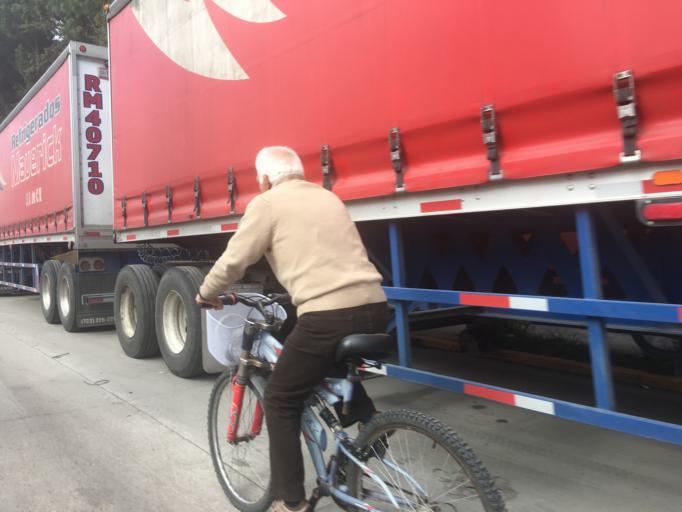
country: MX
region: Mexico
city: Santa Maria Totoltepec
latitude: 19.2900
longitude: -99.5940
